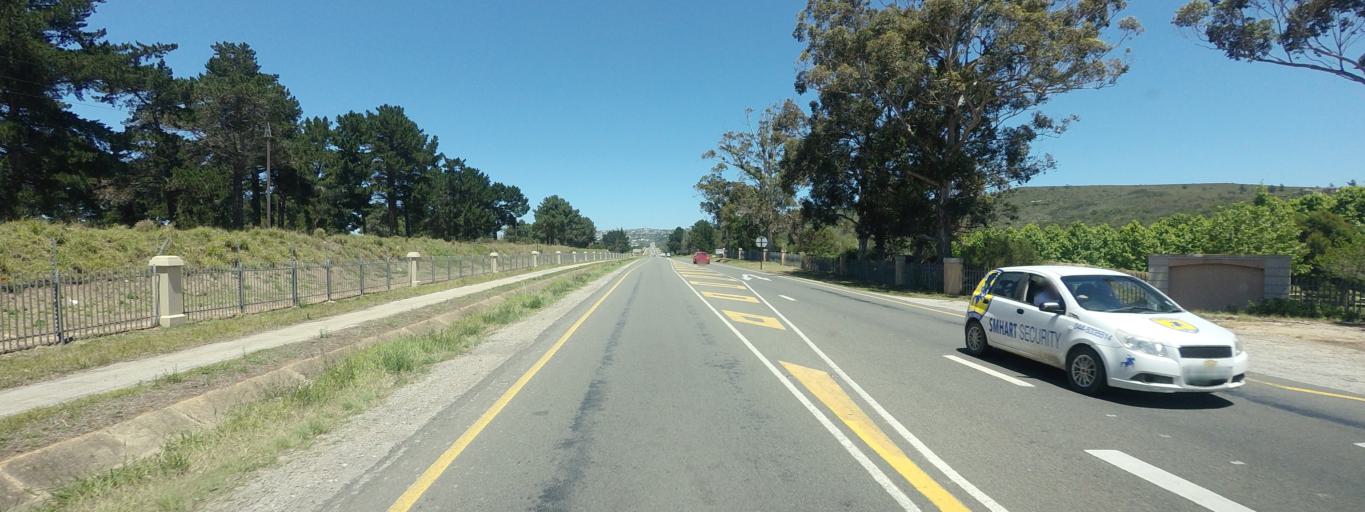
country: ZA
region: Western Cape
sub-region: Eden District Municipality
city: Plettenberg Bay
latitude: -34.0228
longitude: 23.3814
